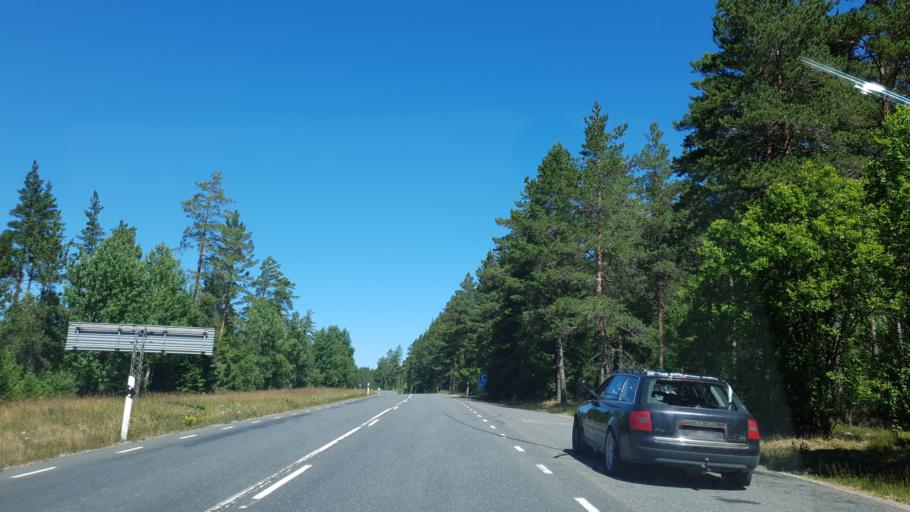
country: SE
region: Joenkoeping
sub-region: Vaggeryds Kommun
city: Vaggeryd
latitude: 57.5250
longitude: 14.1378
